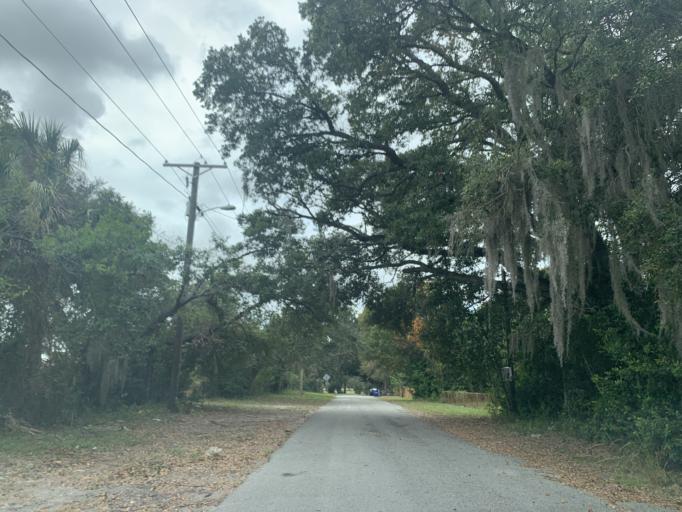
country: US
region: Florida
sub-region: Hillsborough County
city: East Lake-Orient Park
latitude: 27.9797
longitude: -82.4042
